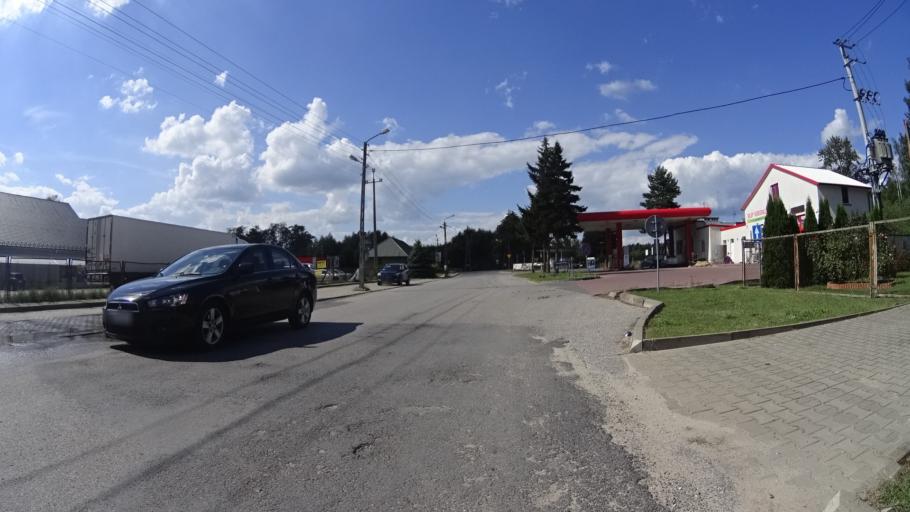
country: PL
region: Masovian Voivodeship
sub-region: Powiat grojecki
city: Mogielnica
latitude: 51.6961
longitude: 20.7279
